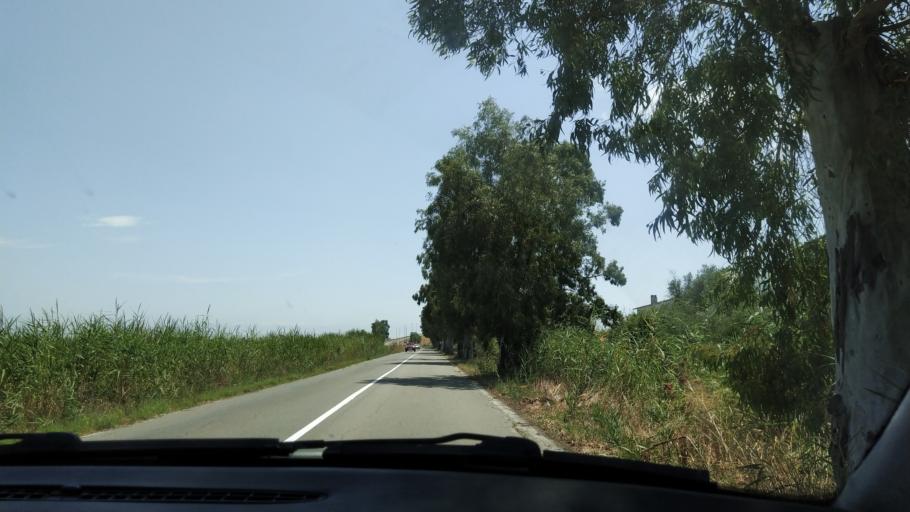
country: IT
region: Basilicate
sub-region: Provincia di Matera
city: Marconia
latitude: 40.3376
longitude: 16.7695
